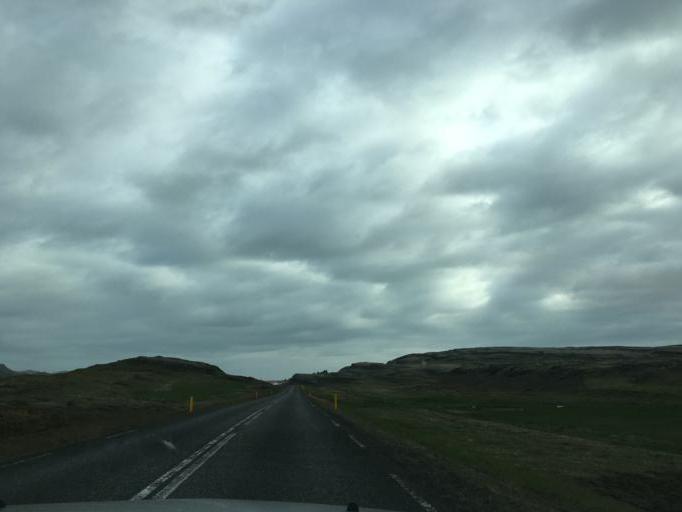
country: IS
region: South
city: Vestmannaeyjar
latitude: 64.2075
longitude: -20.2707
